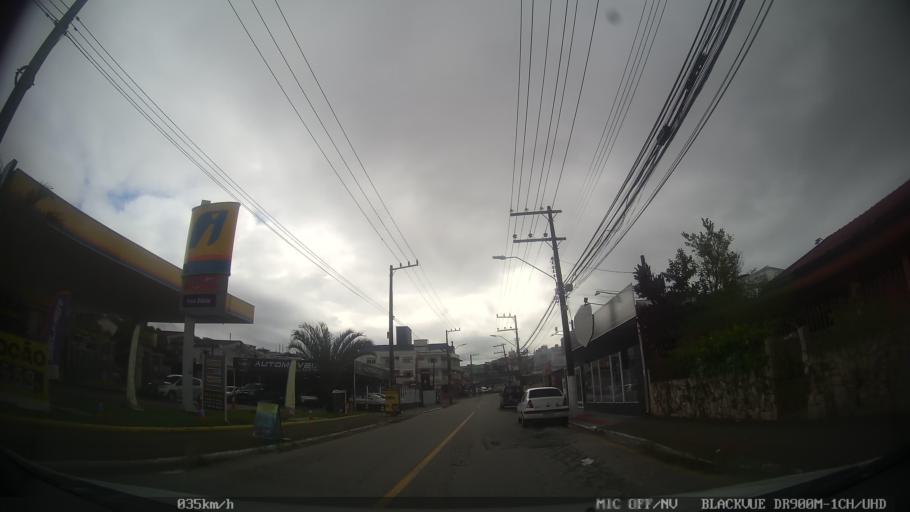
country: BR
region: Santa Catarina
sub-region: Sao Jose
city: Campinas
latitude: -27.5934
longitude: -48.6222
